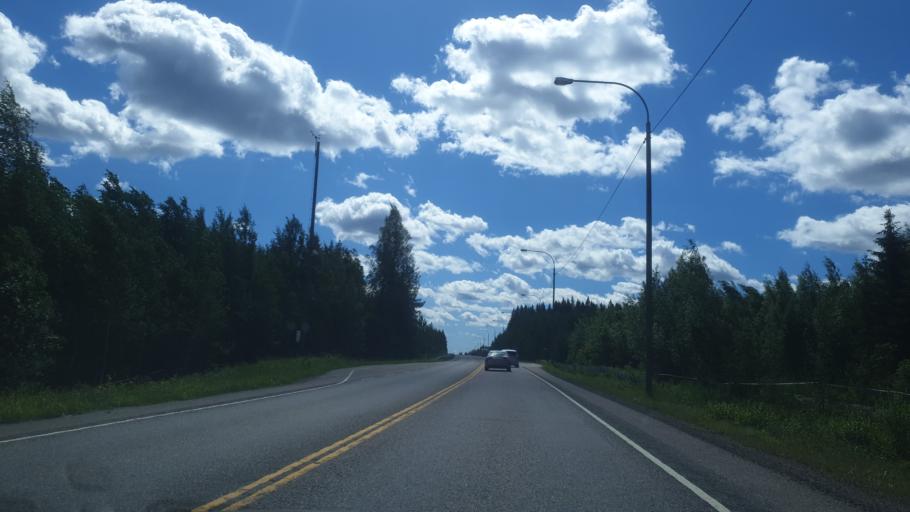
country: FI
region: Northern Savo
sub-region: Varkaus
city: Varkaus
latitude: 62.3840
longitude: 27.8094
